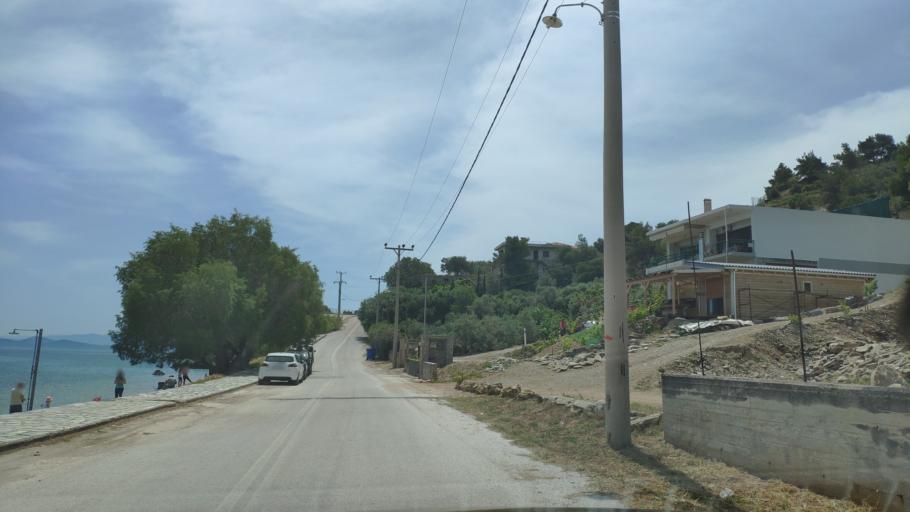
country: GR
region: Attica
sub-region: Nomarchia Anatolikis Attikis
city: Grammatiko
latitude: 38.2659
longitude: 23.9733
